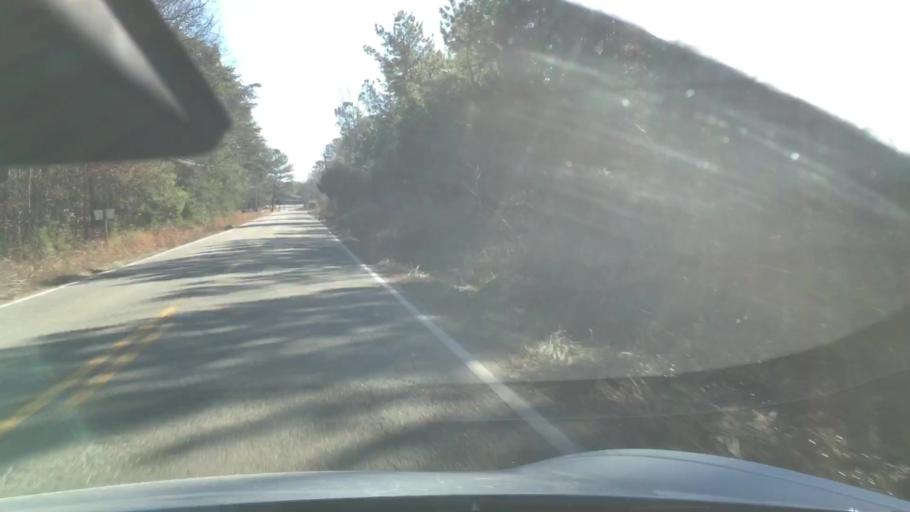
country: US
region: Virginia
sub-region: Henrico County
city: Short Pump
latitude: 37.5708
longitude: -77.7152
